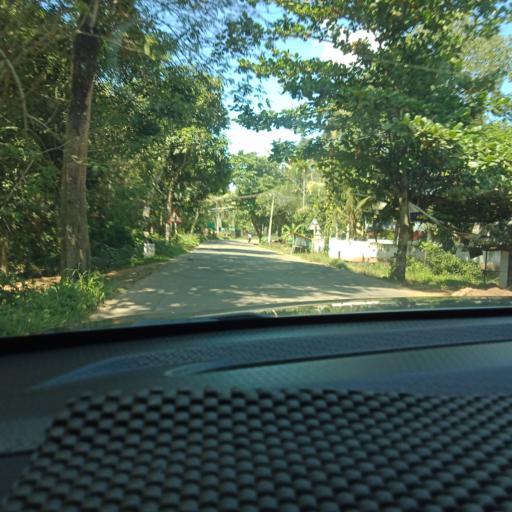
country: IN
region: Kerala
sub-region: Alappuzha
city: Mavelikara
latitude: 9.3003
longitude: 76.4559
